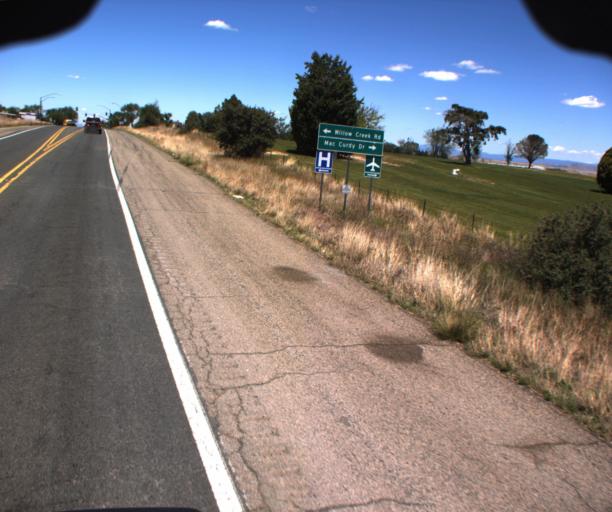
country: US
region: Arizona
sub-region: Yavapai County
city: Prescott
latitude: 34.6417
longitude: -112.4318
